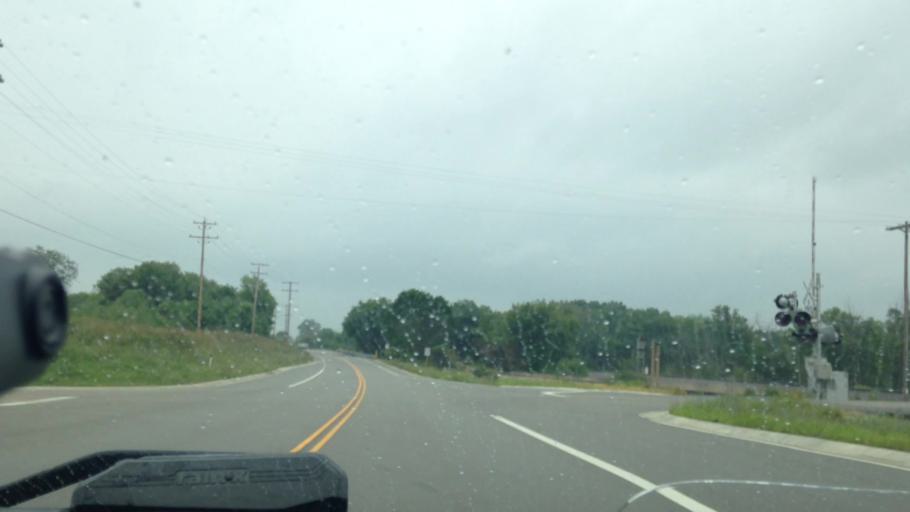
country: US
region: Wisconsin
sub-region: Washington County
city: Slinger
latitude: 43.3040
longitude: -88.2413
